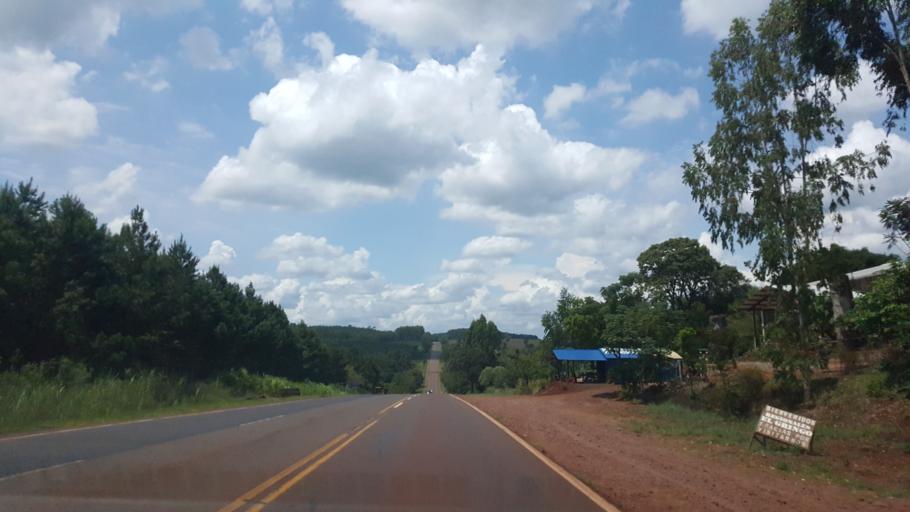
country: AR
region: Misiones
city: Garuhape
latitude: -26.8111
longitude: -54.9341
